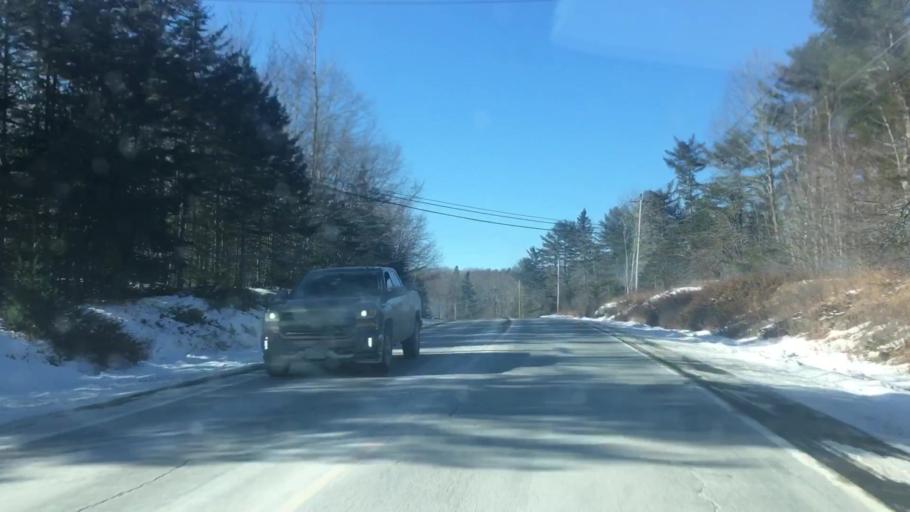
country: US
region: Maine
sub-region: Hancock County
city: Surry
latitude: 44.4946
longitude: -68.4691
